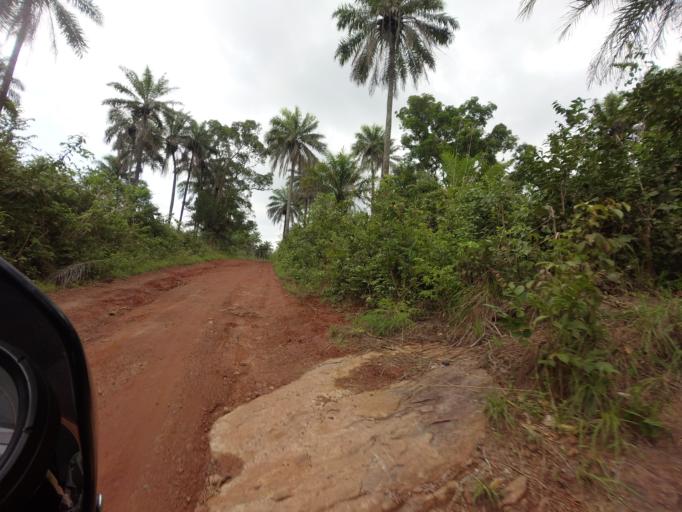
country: SL
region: Northern Province
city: Kambia
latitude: 9.0960
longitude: -13.0129
